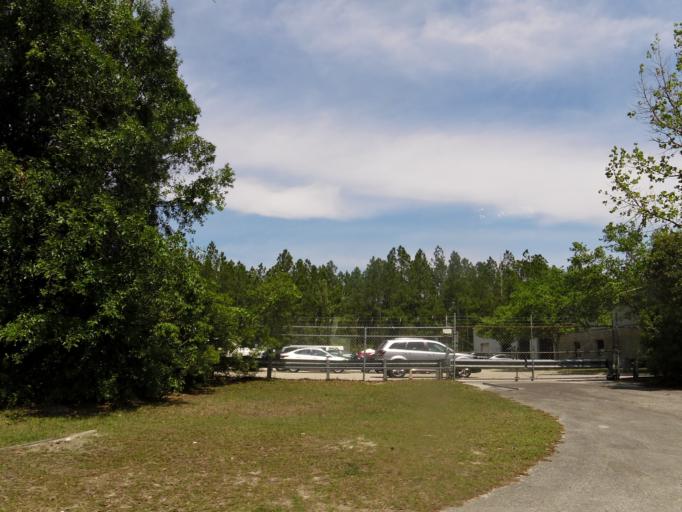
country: US
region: Florida
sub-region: Nassau County
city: Nassau Village-Ratliff
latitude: 30.4951
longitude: -81.6684
